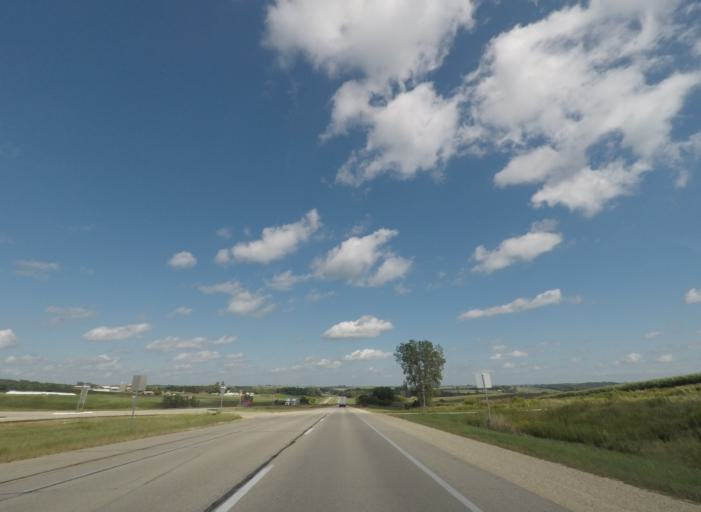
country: US
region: Iowa
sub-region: Dubuque County
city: Cascade
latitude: 42.3162
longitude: -90.9414
